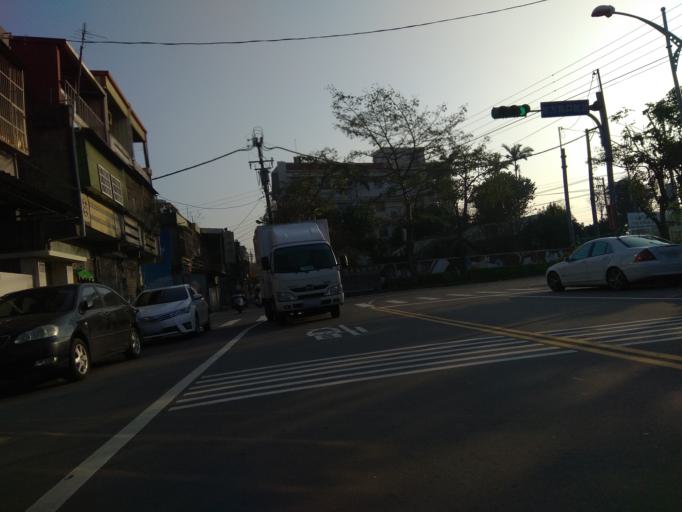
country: TW
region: Taiwan
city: Daxi
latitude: 24.9159
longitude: 121.1865
